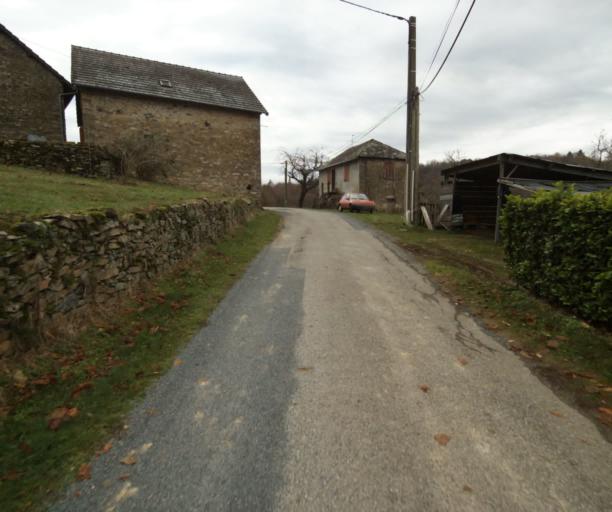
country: FR
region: Limousin
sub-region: Departement de la Correze
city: Sainte-Fortunade
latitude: 45.2250
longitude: 1.7596
